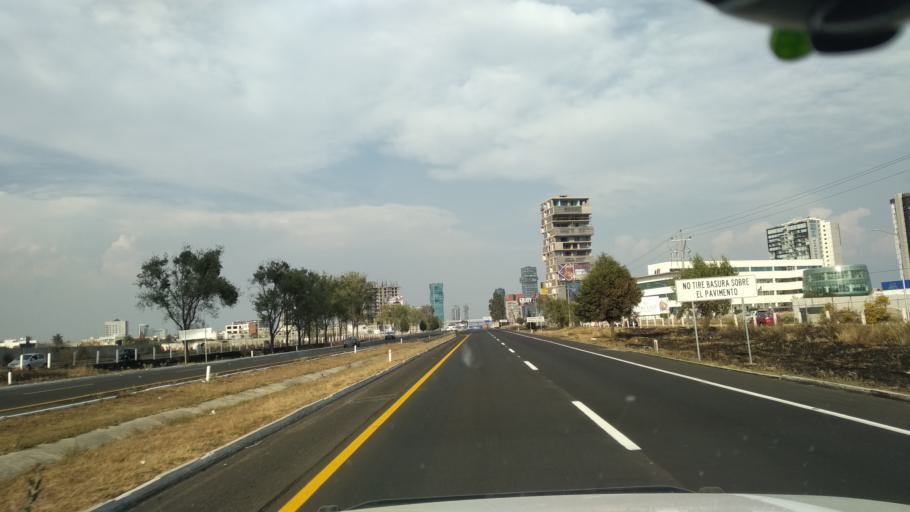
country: MX
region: Puebla
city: Tlazcalancingo
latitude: 19.0008
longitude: -98.2778
